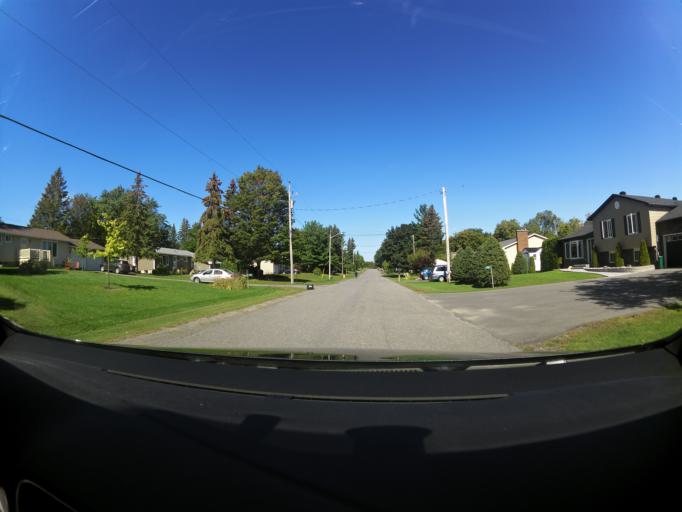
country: CA
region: Ontario
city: Bells Corners
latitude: 45.2743
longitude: -75.9465
